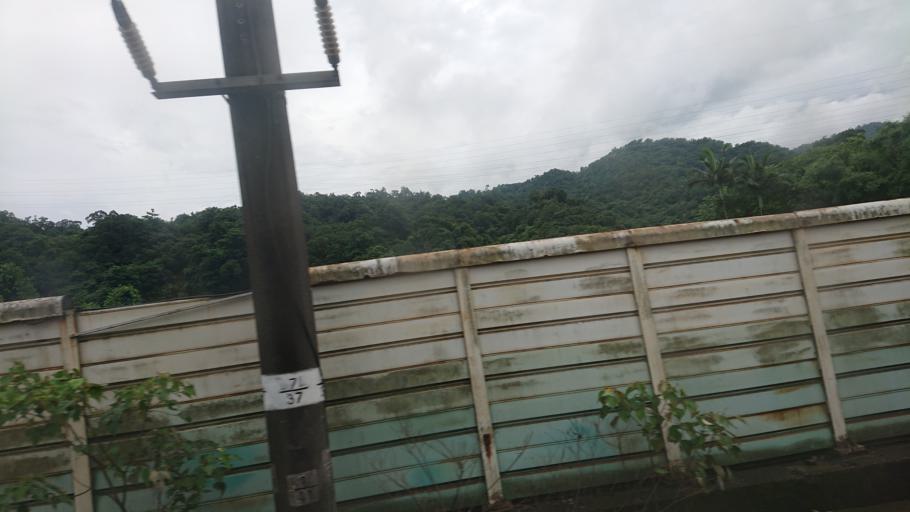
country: TW
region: Taiwan
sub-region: Keelung
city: Keelung
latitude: 25.0813
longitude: 121.7029
